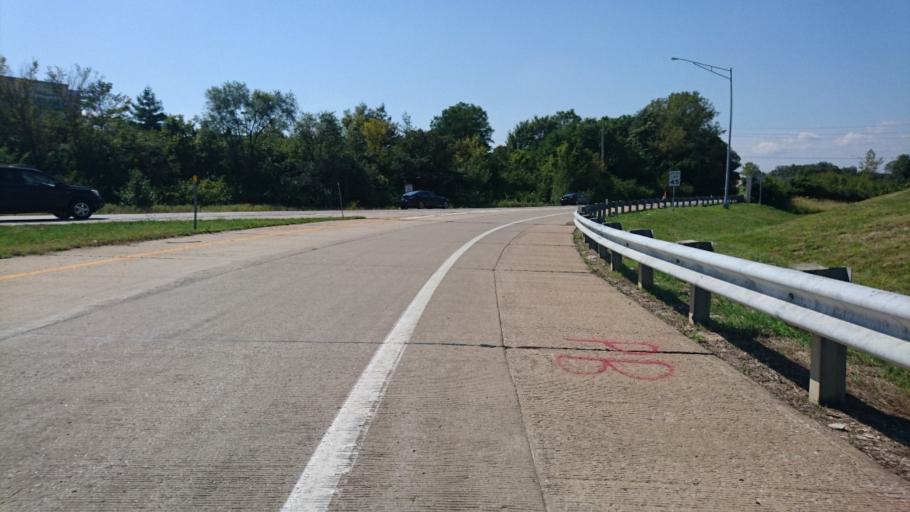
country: US
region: Missouri
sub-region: Saint Louis County
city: Town and Country
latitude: 38.6043
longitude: -90.4568
